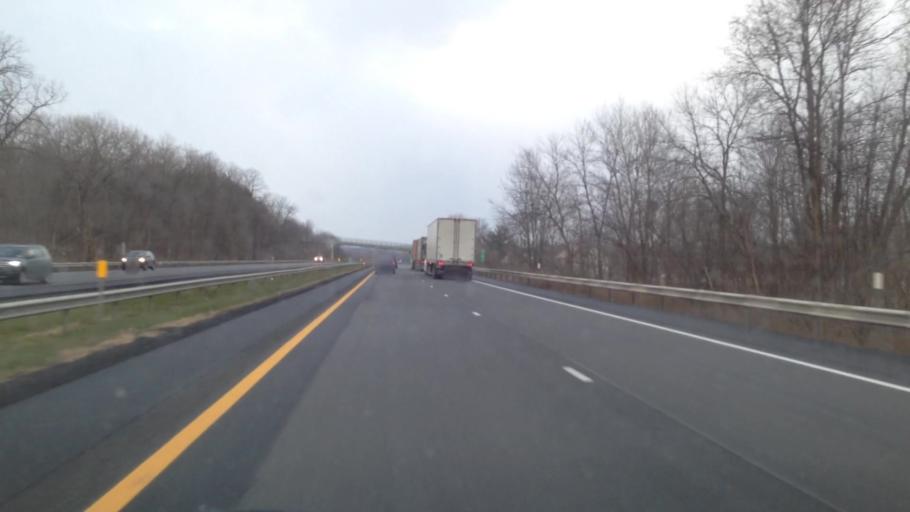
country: US
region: New York
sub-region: Montgomery County
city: Fonda
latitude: 42.9391
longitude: -74.3369
